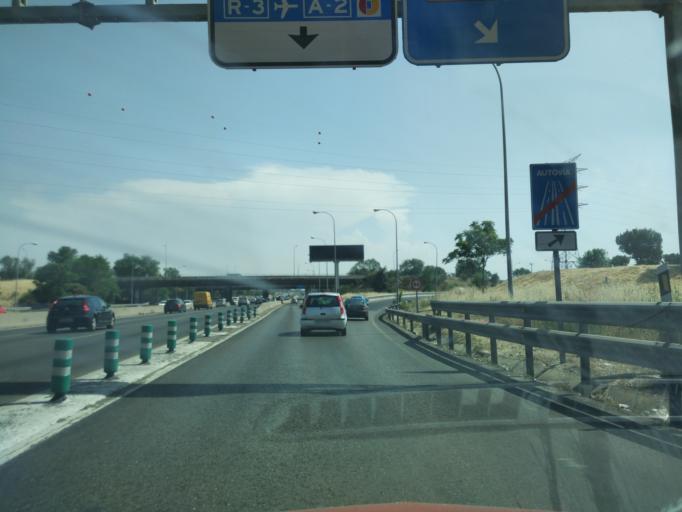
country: ES
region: Madrid
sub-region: Provincia de Madrid
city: Carabanchel
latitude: 40.3677
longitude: -3.7206
